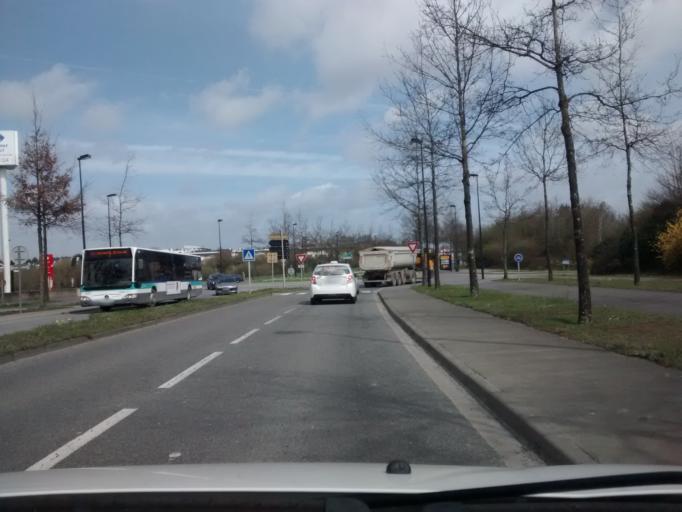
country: FR
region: Brittany
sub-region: Departement d'Ille-et-Vilaine
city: Saint-Jacques-de-la-Lande
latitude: 48.0816
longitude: -1.7119
